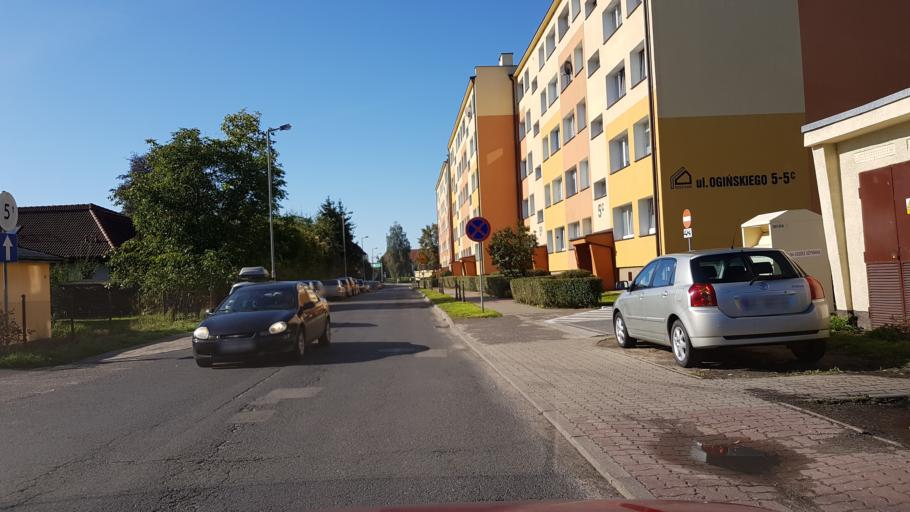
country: PL
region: West Pomeranian Voivodeship
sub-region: Koszalin
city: Koszalin
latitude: 54.1928
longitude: 16.2148
